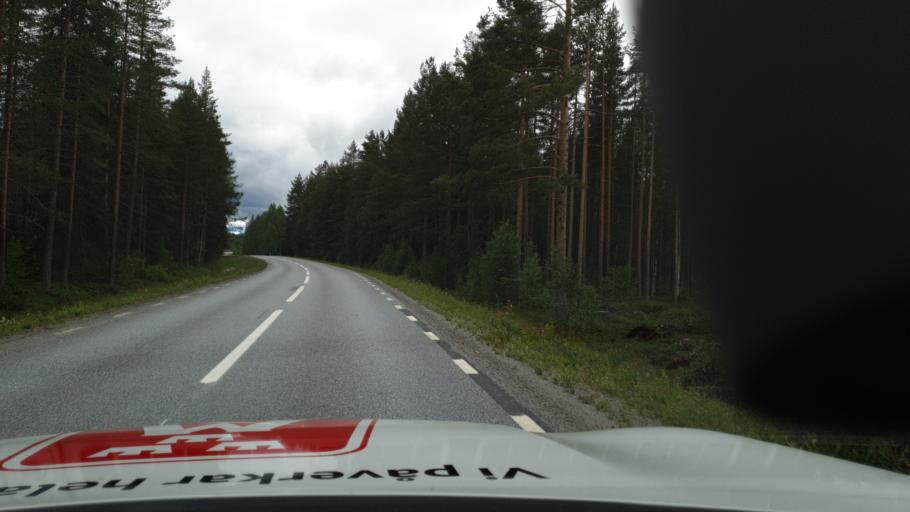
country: SE
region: Vaesterbotten
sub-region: Skelleftea Kommun
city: Burtraesk
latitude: 64.4072
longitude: 20.3895
